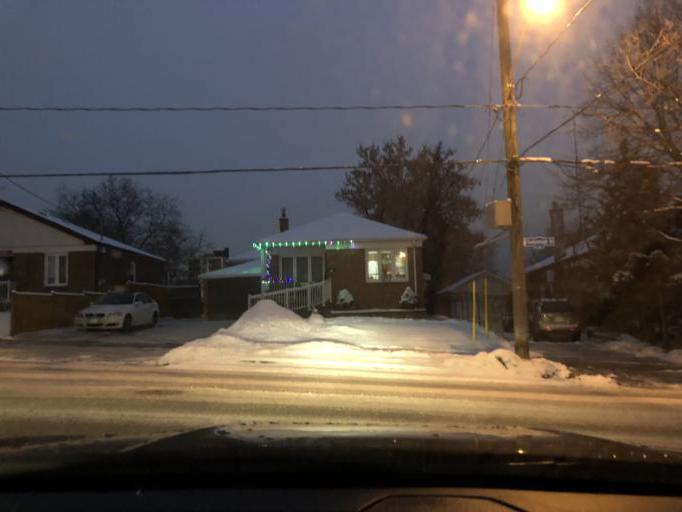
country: CA
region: Ontario
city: Toronto
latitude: 43.7019
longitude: -79.4788
